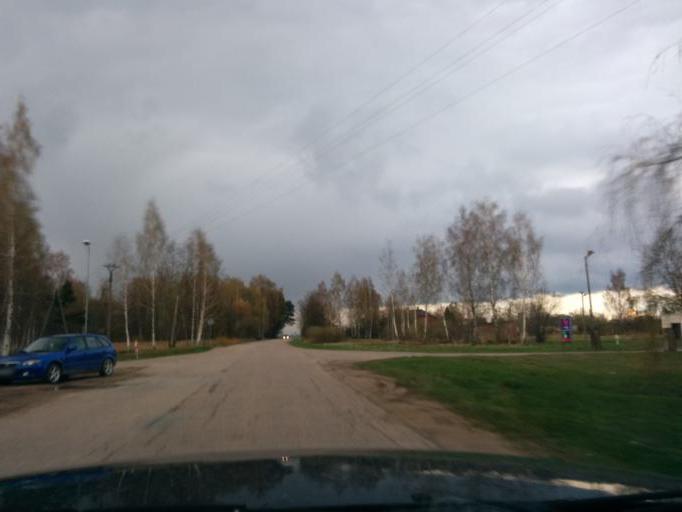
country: LV
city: Tervete
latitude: 56.4175
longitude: 23.5557
